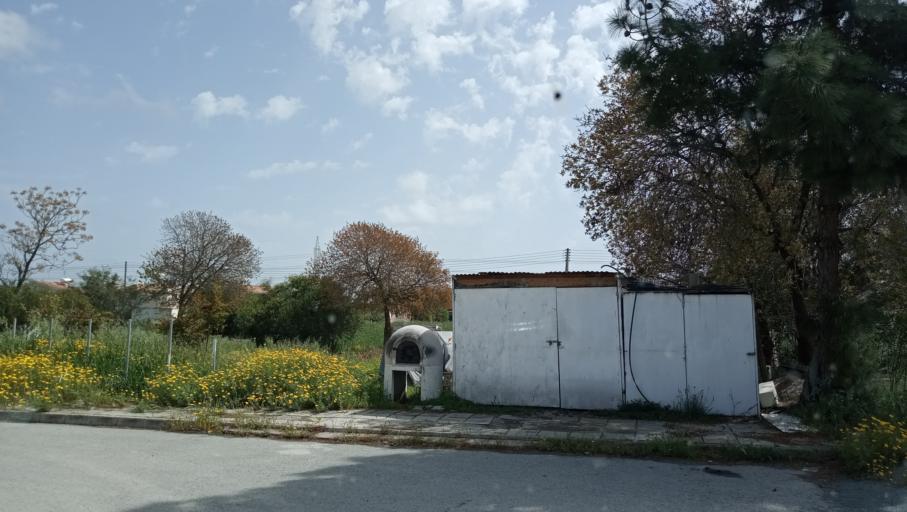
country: CY
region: Lefkosia
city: Dali
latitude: 35.0229
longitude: 33.4324
